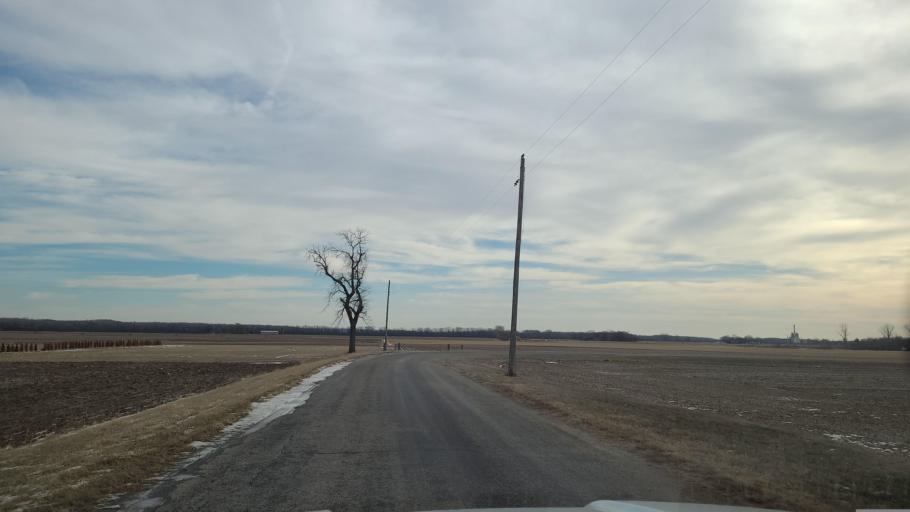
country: US
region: Kansas
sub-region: Douglas County
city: Lawrence
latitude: 39.0297
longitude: -95.3134
